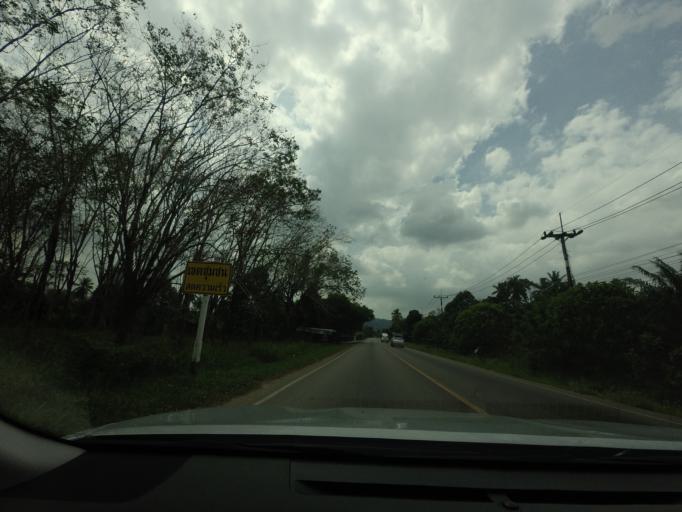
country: TH
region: Phangnga
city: Ban Ao Nang
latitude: 8.1244
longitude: 98.8049
